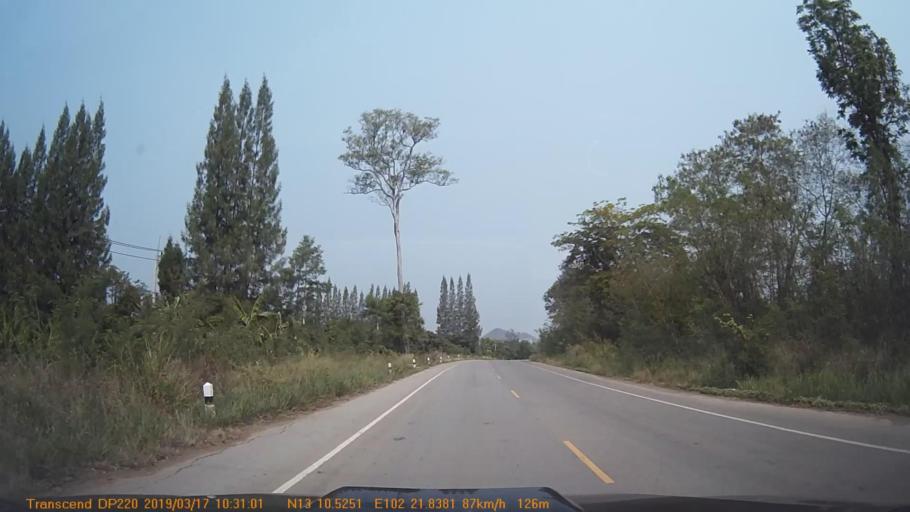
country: TH
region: Chanthaburi
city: Soi Dao
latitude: 13.1757
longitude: 102.3638
